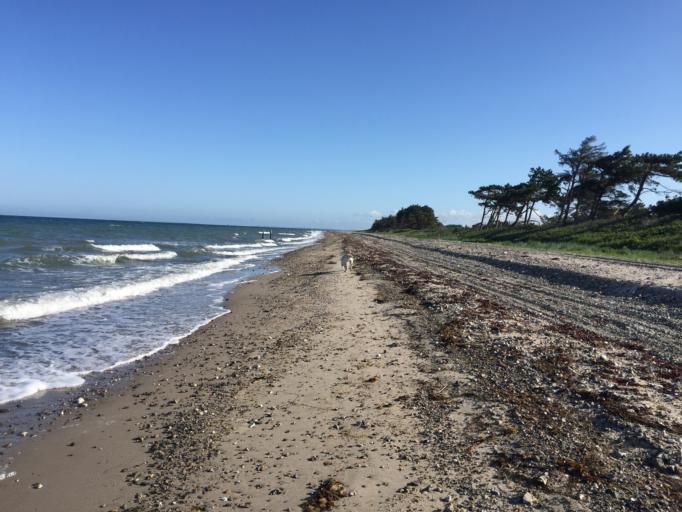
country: DK
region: Zealand
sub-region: Slagelse Kommune
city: Korsor
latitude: 55.2100
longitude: 11.1728
